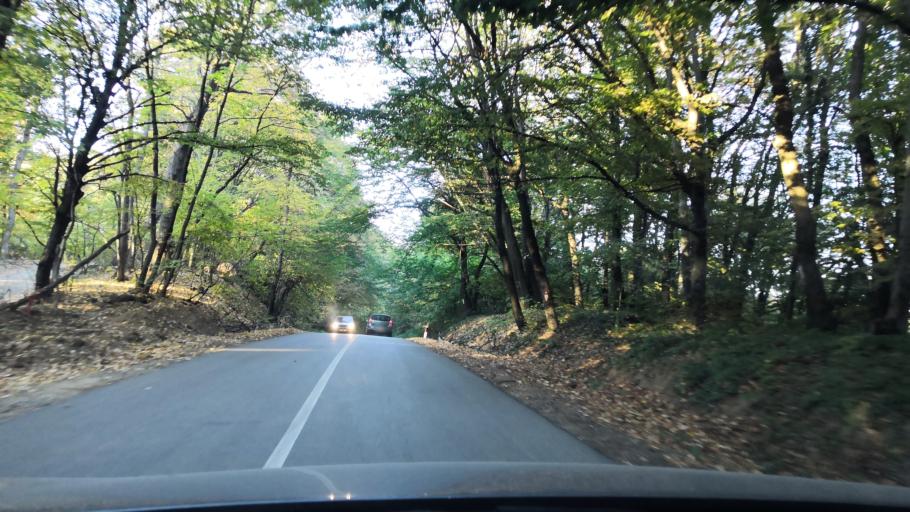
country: RS
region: Autonomna Pokrajina Vojvodina
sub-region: Sremski Okrug
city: Irig
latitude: 45.1557
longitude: 19.8550
